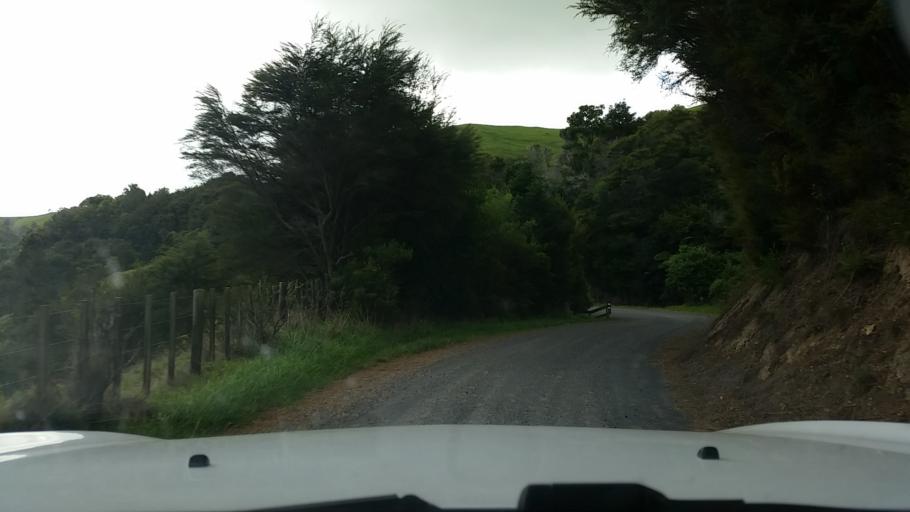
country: NZ
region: Waikato
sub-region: Hauraki District
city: Ngatea
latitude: -37.4779
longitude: 175.4545
